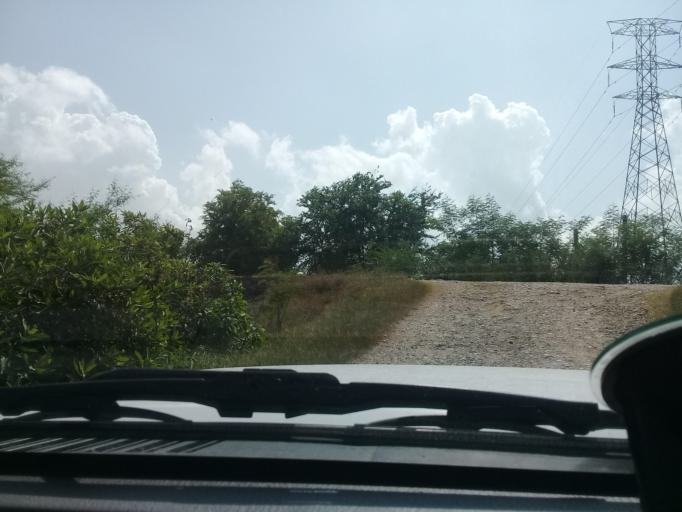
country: MX
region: Veracruz
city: Moralillo
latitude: 22.2270
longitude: -97.8993
